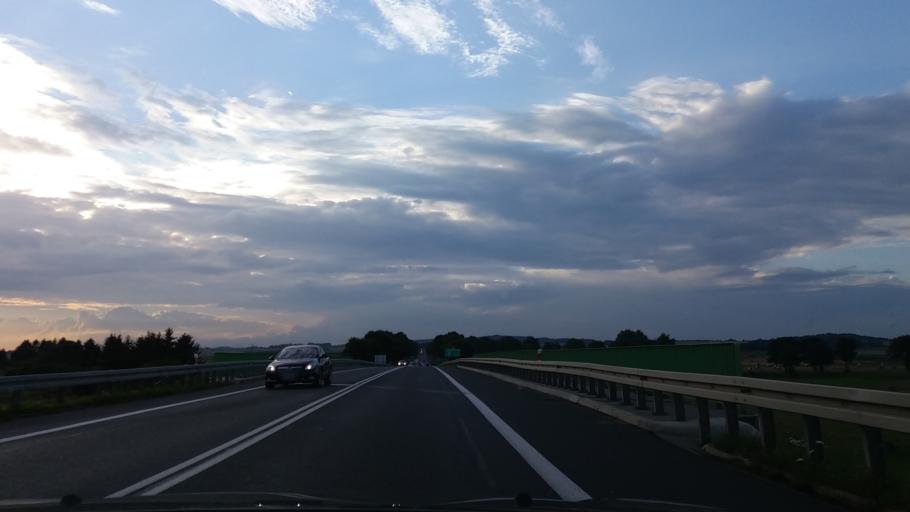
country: PL
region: Lower Silesian Voivodeship
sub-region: Powiat polkowicki
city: Gaworzyce
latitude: 51.6185
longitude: 15.9271
